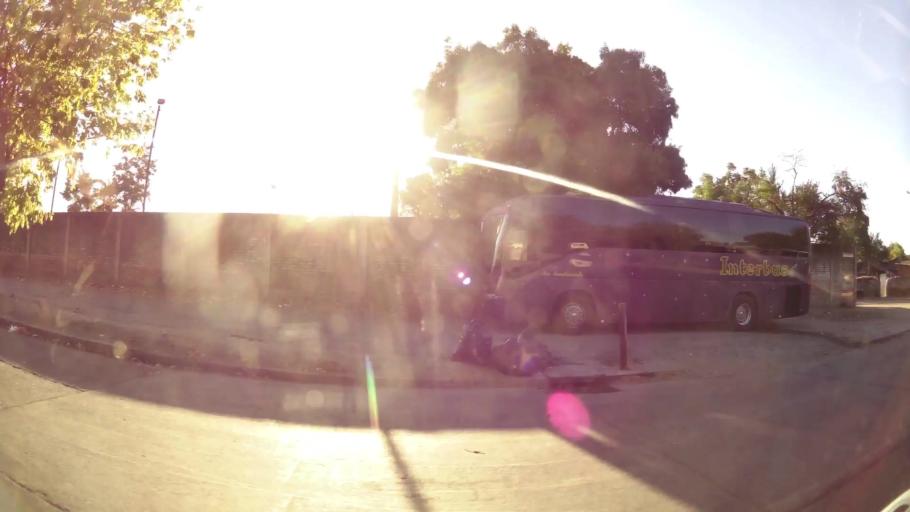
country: CL
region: Maule
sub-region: Provincia de Talca
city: Talca
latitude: -35.4337
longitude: -71.6484
